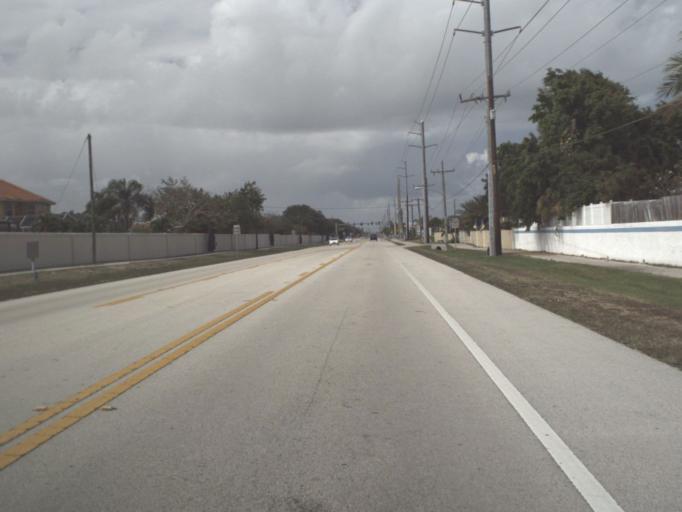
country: US
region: Florida
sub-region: Brevard County
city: Satellite Beach
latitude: 28.1685
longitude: -80.6059
